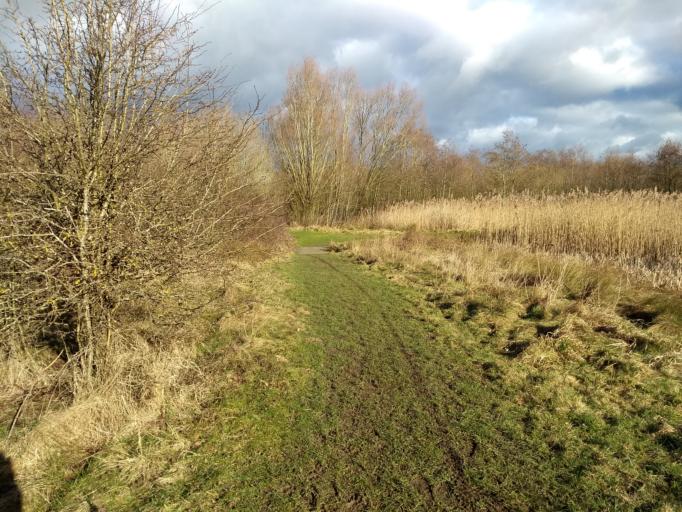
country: GB
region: England
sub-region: Buckinghamshire
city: Bletchley
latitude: 51.9845
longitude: -0.7378
